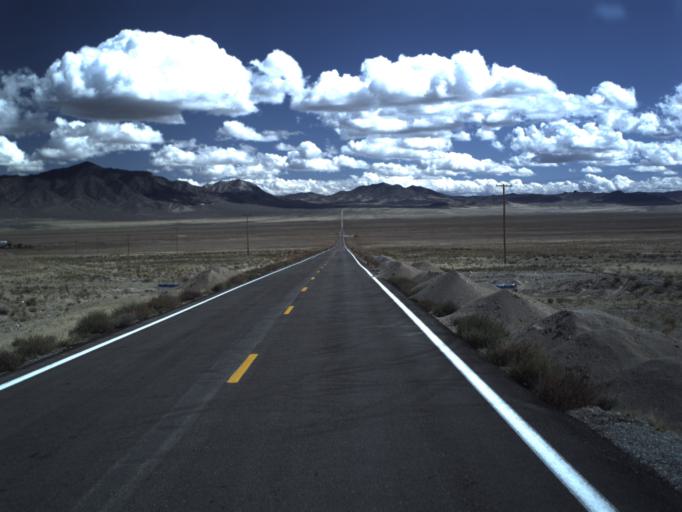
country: US
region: Utah
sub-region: Beaver County
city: Milford
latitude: 38.4855
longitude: -113.4532
